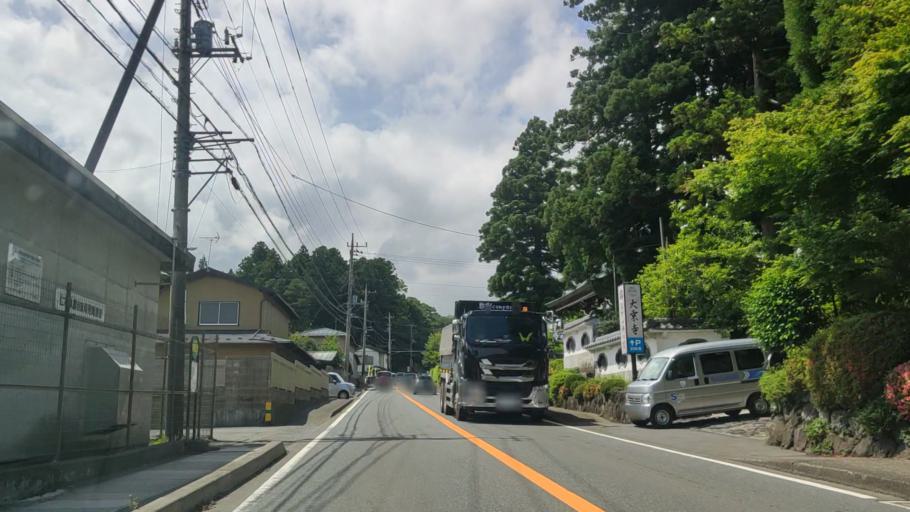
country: JP
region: Shizuoka
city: Gotemba
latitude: 35.3241
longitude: 138.9092
